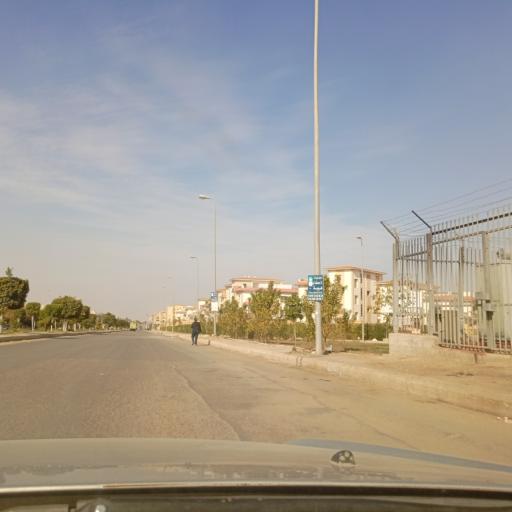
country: EG
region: Muhafazat al Qalyubiyah
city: Al Khankah
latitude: 30.0380
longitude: 31.4852
